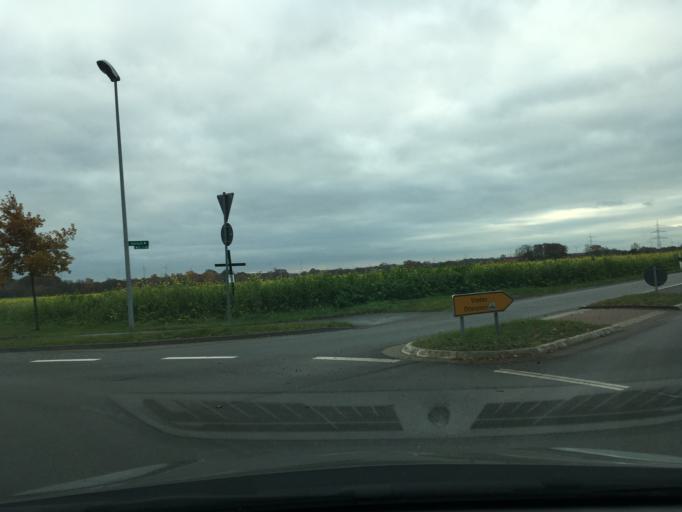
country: DE
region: North Rhine-Westphalia
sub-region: Regierungsbezirk Munster
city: Ahaus
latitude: 52.0878
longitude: 6.9652
